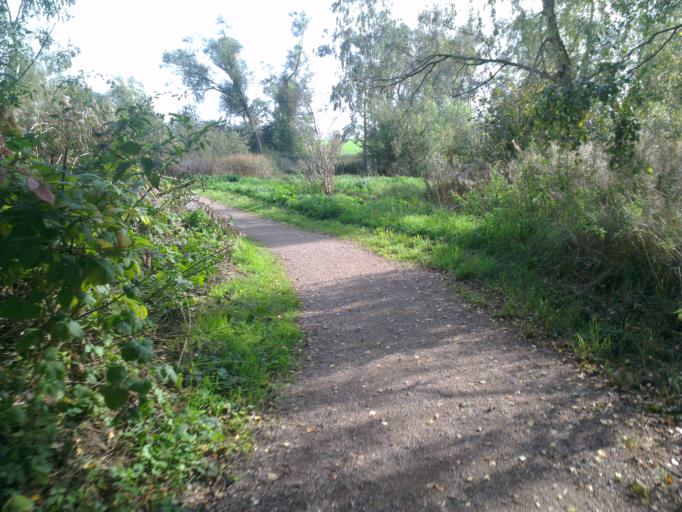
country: DK
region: Capital Region
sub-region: Frederikssund Kommune
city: Frederikssund
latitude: 55.8328
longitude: 12.0874
